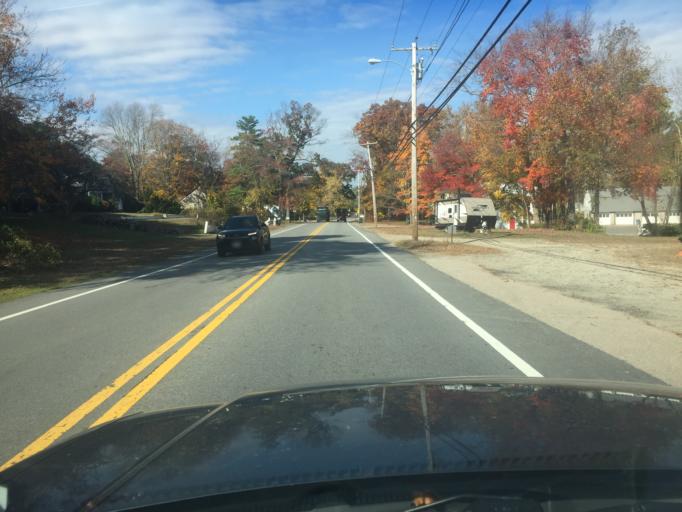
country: US
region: Massachusetts
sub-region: Worcester County
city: Milford
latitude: 42.1116
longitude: -71.5083
